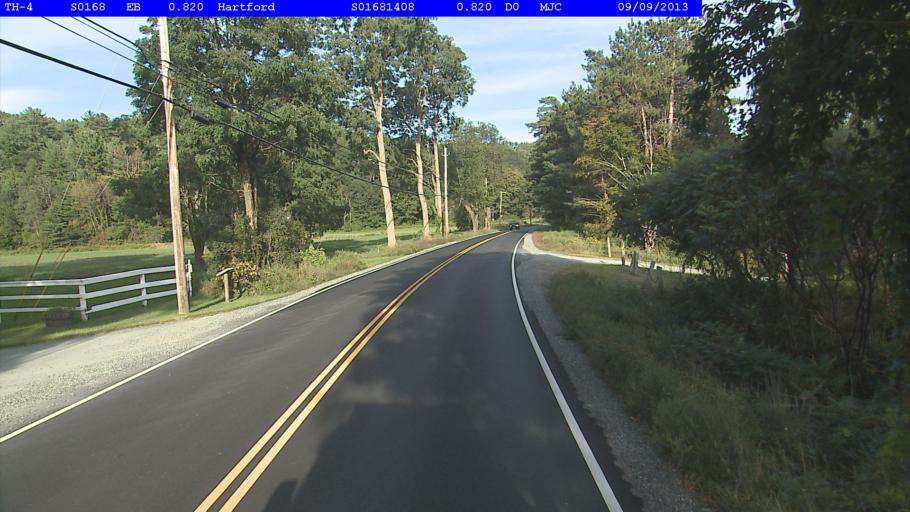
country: US
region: Vermont
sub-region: Windsor County
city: White River Junction
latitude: 43.6482
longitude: -72.4068
